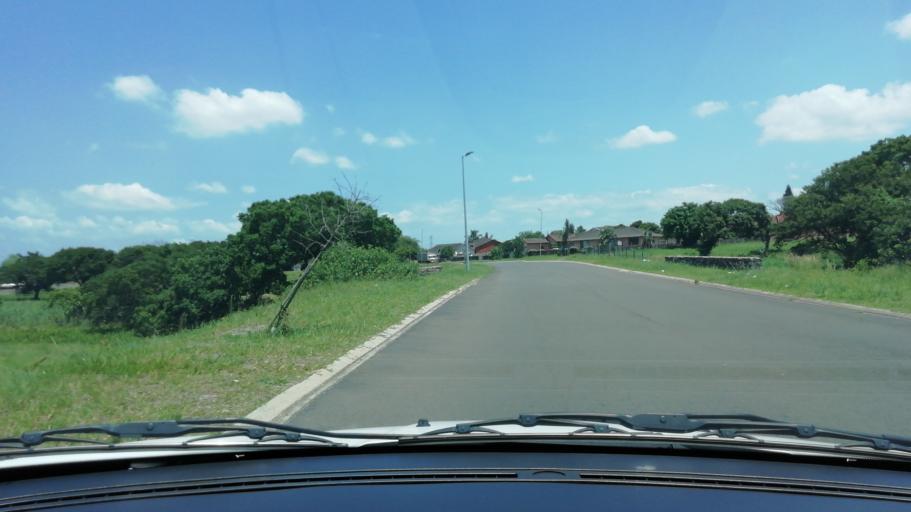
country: ZA
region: KwaZulu-Natal
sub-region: uThungulu District Municipality
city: Richards Bay
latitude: -28.7333
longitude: 32.0485
